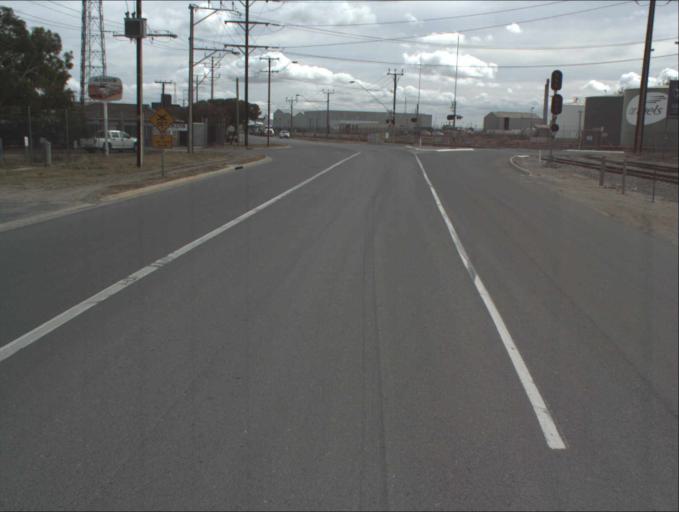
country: AU
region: South Australia
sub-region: Port Adelaide Enfield
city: Birkenhead
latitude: -34.8226
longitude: 138.5062
